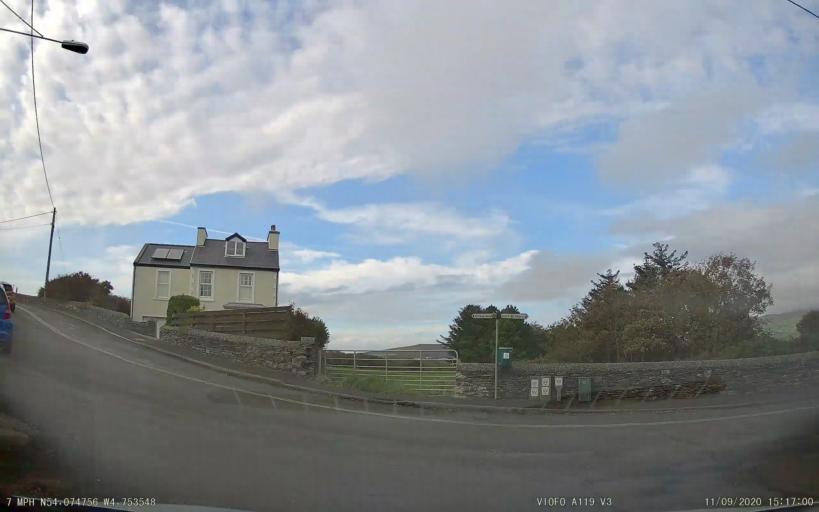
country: IM
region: Port Erin
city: Port Erin
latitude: 54.0747
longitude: -4.7535
